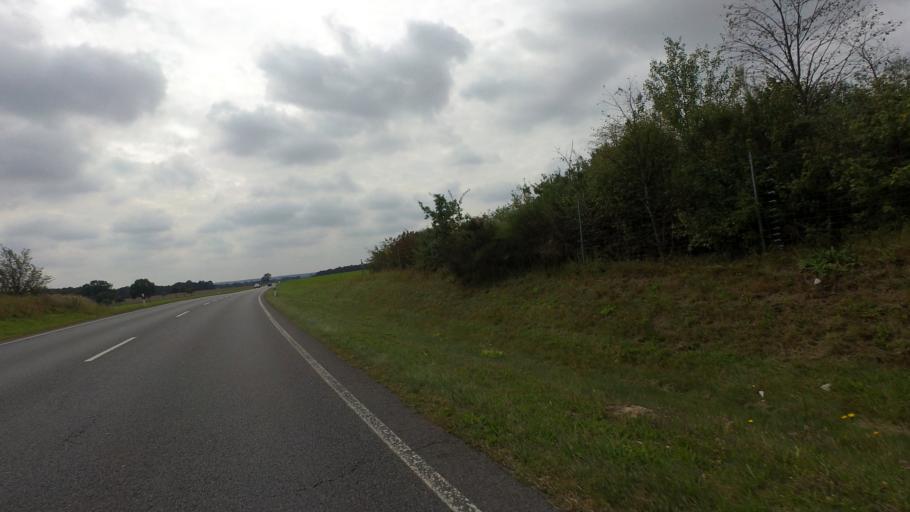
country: DE
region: Brandenburg
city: Luckau
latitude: 51.8271
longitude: 13.6856
